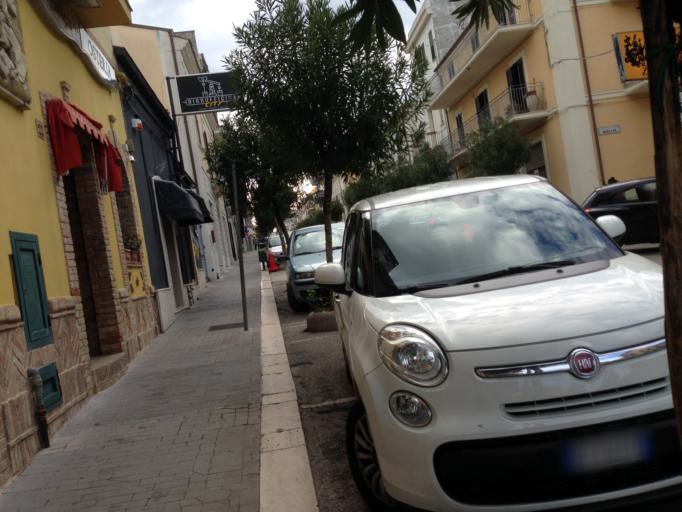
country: IT
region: Molise
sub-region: Provincia di Campobasso
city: Termoli
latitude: 42.0034
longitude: 14.9969
